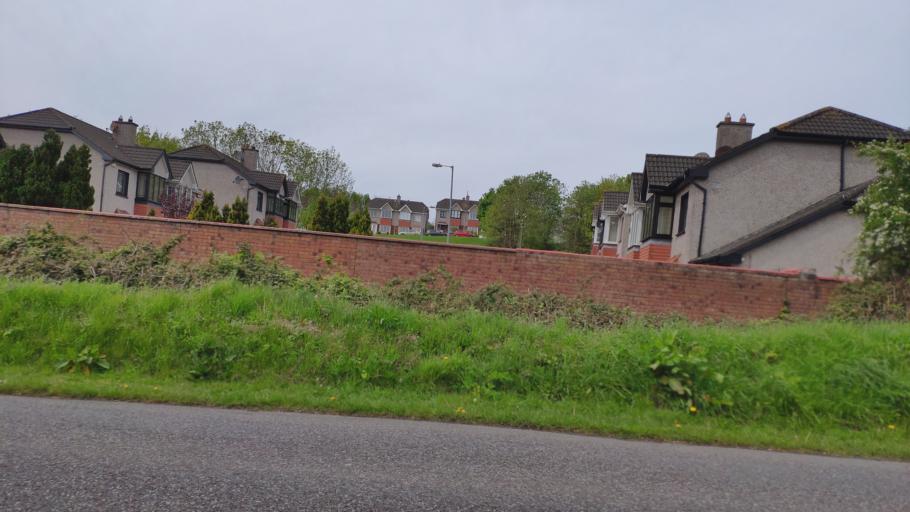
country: IE
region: Munster
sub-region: County Cork
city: Cork
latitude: 51.9241
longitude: -8.4560
